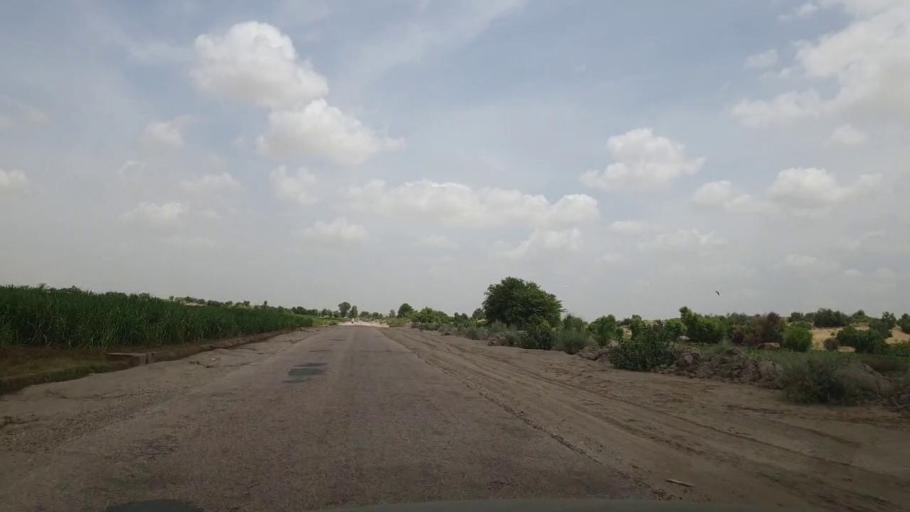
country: PK
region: Sindh
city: Kot Diji
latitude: 27.2169
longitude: 69.1027
